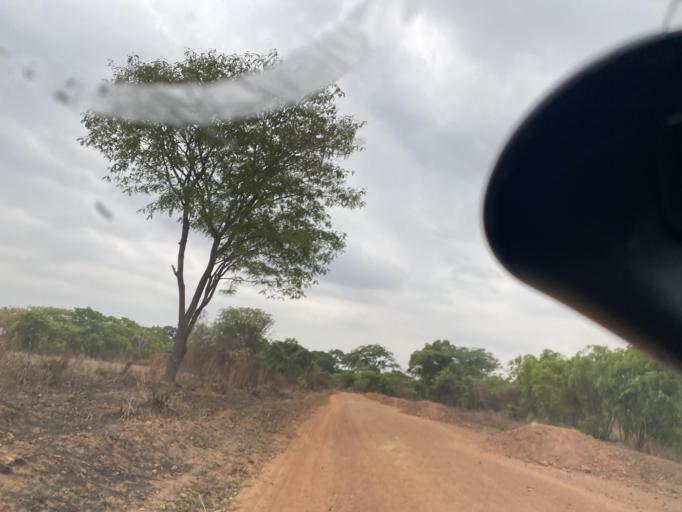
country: ZM
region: Lusaka
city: Chongwe
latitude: -15.2410
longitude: 28.7195
